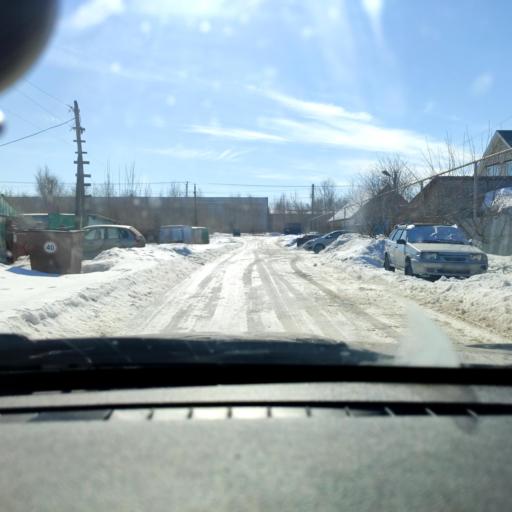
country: RU
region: Samara
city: Tol'yatti
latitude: 53.5663
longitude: 49.3221
